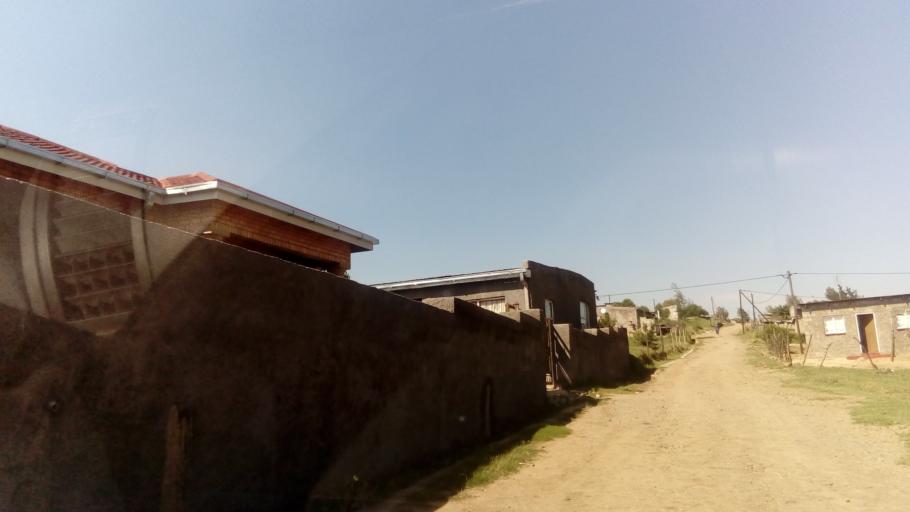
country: LS
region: Berea
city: Teyateyaneng
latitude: -29.1446
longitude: 27.7576
